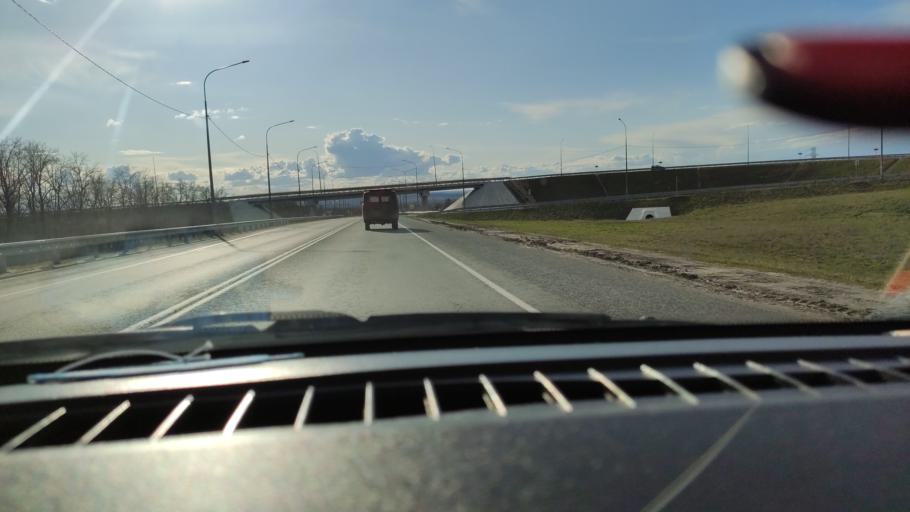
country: RU
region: Saratov
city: Yelshanka
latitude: 51.8256
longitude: 46.2902
